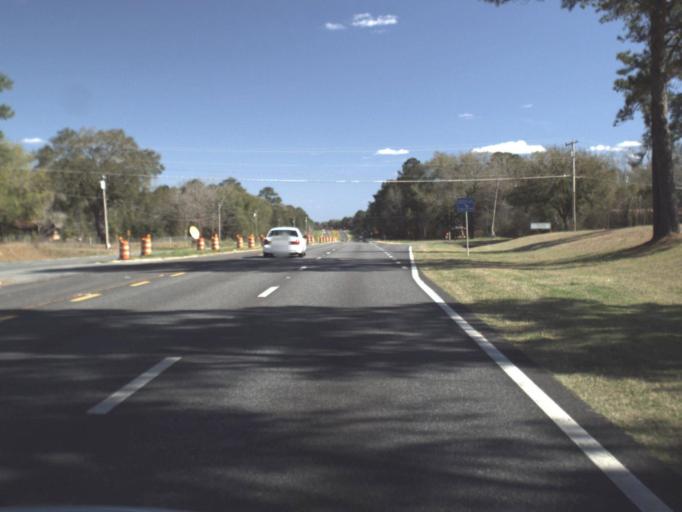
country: US
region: Florida
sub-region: Gadsden County
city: Quincy
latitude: 30.5696
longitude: -84.5480
